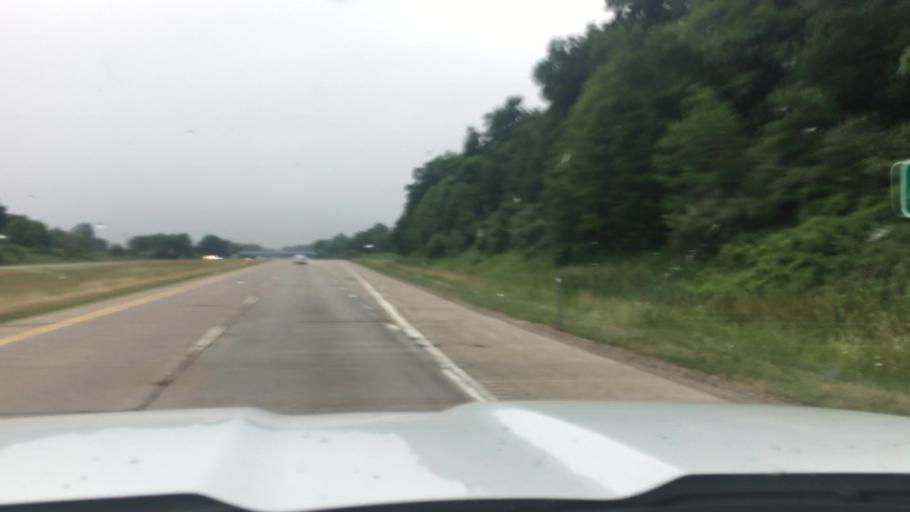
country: US
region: Michigan
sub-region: Clinton County
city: DeWitt
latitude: 42.8073
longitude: -84.6129
